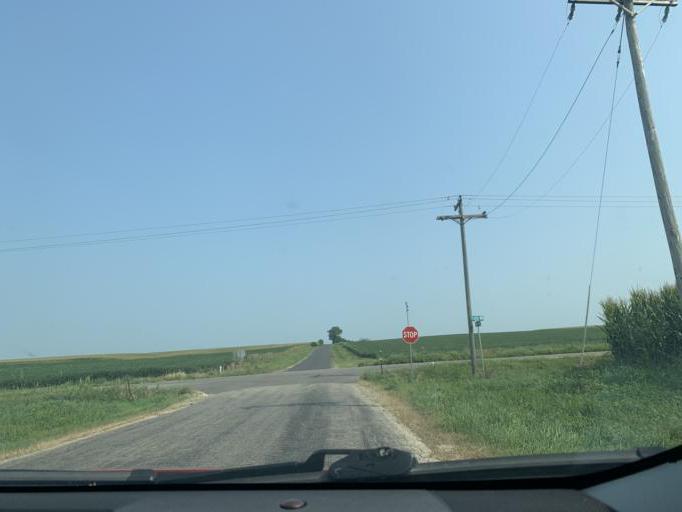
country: US
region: Illinois
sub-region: Whiteside County
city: Sterling
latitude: 41.8438
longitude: -89.7469
